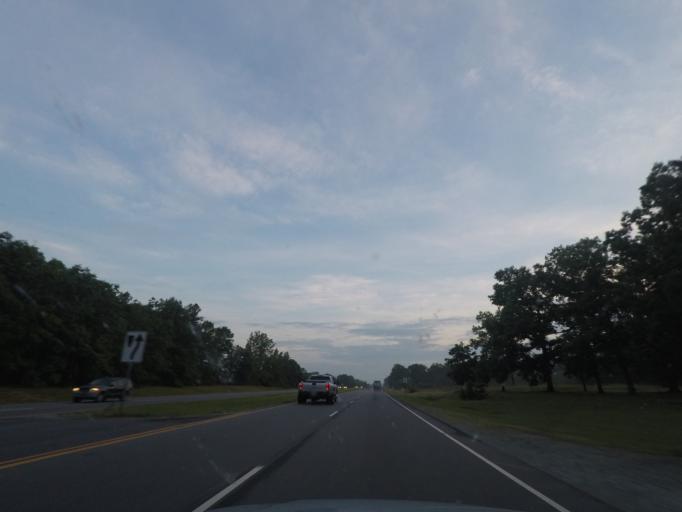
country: US
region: North Carolina
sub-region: Person County
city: Roxboro
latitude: 36.2254
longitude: -78.9293
